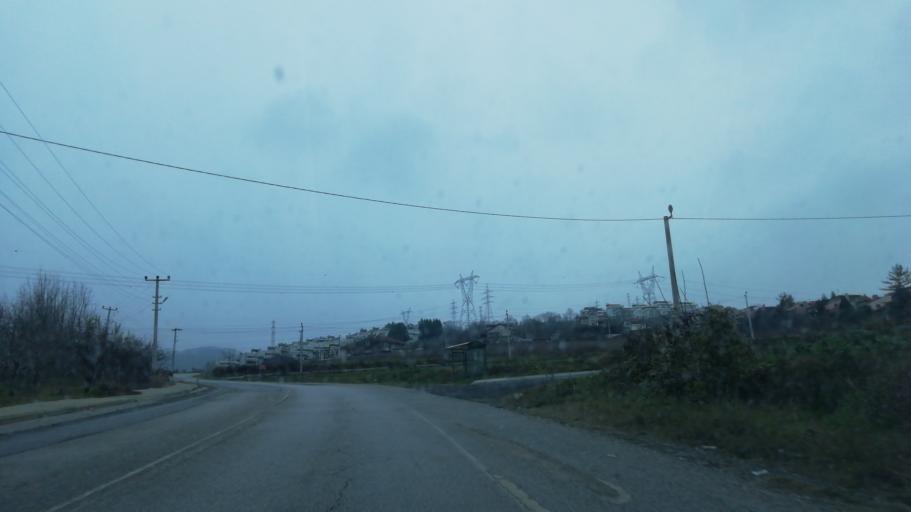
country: TR
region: Sakarya
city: Kazimpasa
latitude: 40.7415
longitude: 30.3085
